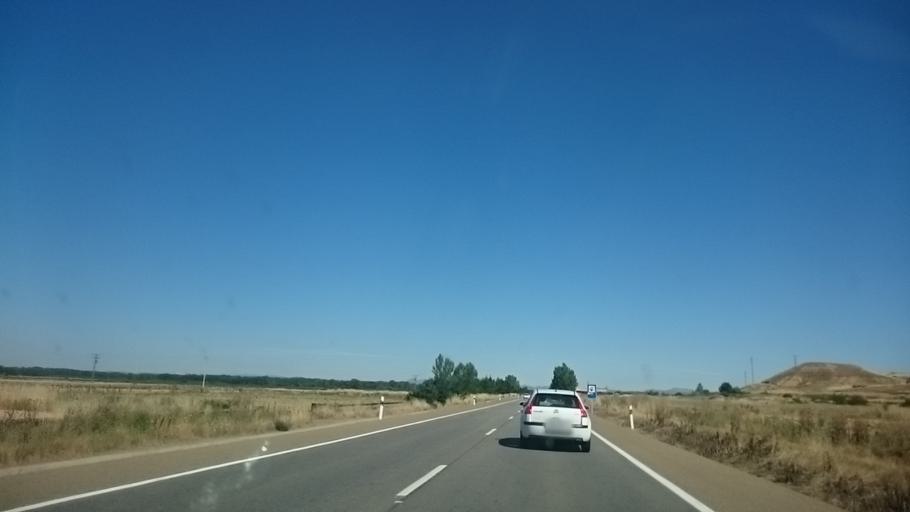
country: ES
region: Castille and Leon
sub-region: Provincia de Leon
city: Mansilla Mayor
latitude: 42.5188
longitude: -5.4326
